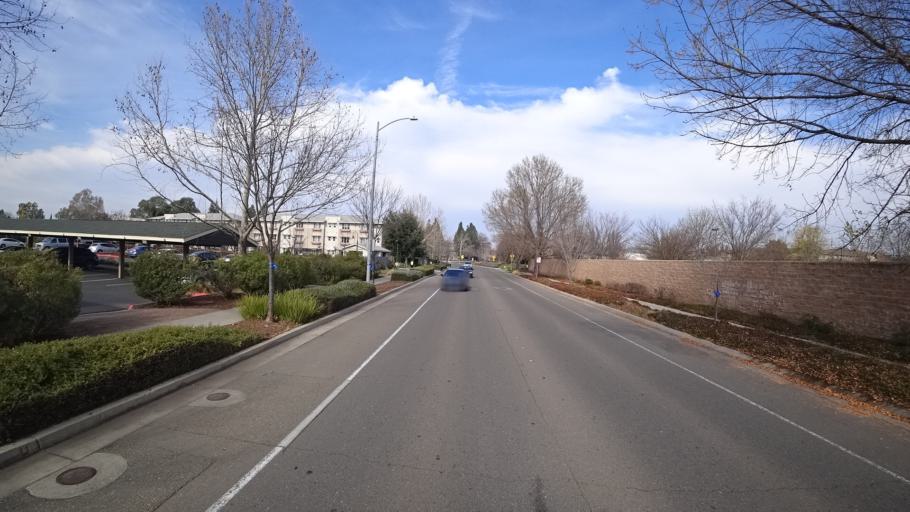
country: US
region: California
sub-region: Yolo County
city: Davis
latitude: 38.5500
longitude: -121.7200
